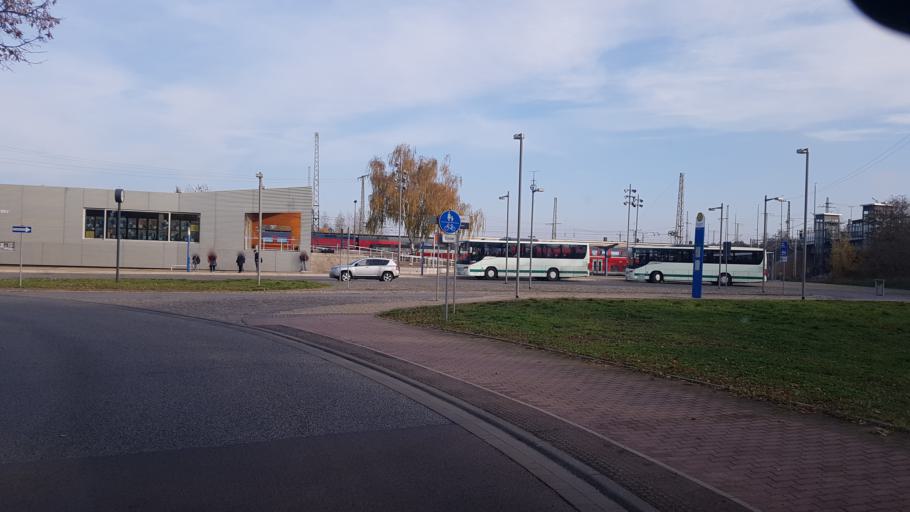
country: DE
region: Brandenburg
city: Falkenberg
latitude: 51.5837
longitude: 13.2458
